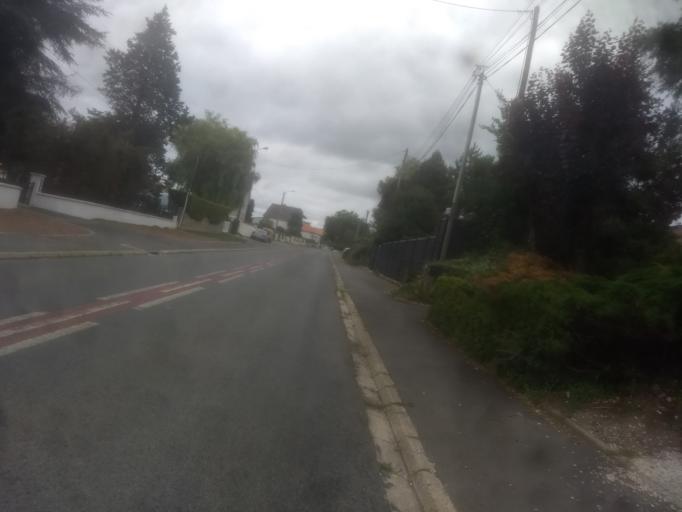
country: FR
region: Nord-Pas-de-Calais
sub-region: Departement du Pas-de-Calais
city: Neuville-Saint-Vaast
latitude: 50.3535
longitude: 2.7518
